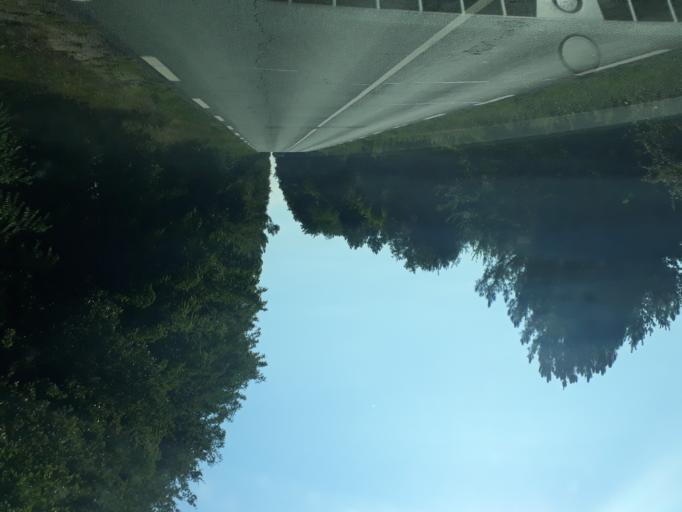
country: FR
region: Centre
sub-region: Departement du Loir-et-Cher
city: Chatillon-sur-Cher
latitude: 47.2883
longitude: 1.5234
